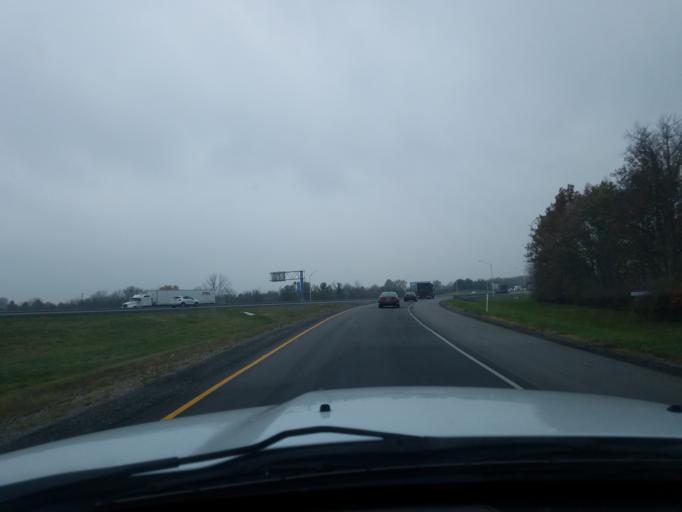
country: US
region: Indiana
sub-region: Johnson County
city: Franklin
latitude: 39.4853
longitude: -86.0137
